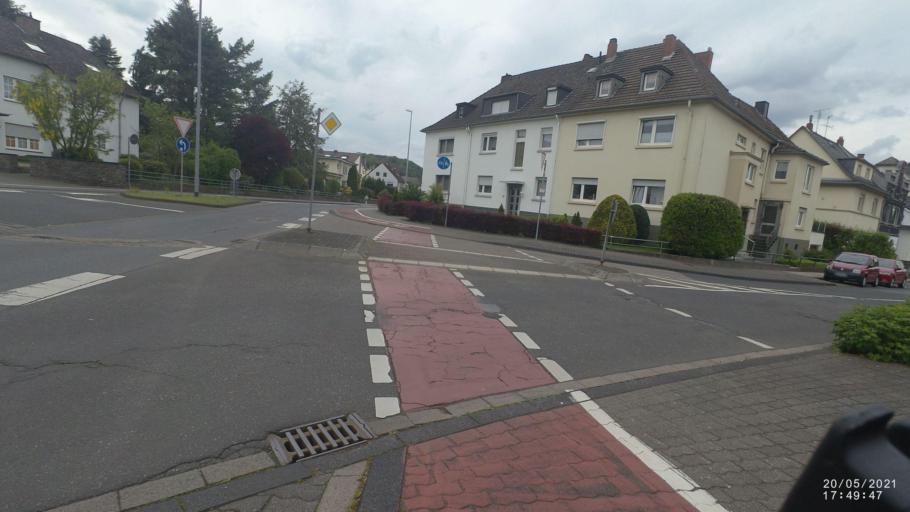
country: DE
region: Rheinland-Pfalz
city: Andernach
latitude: 50.4322
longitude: 7.4031
